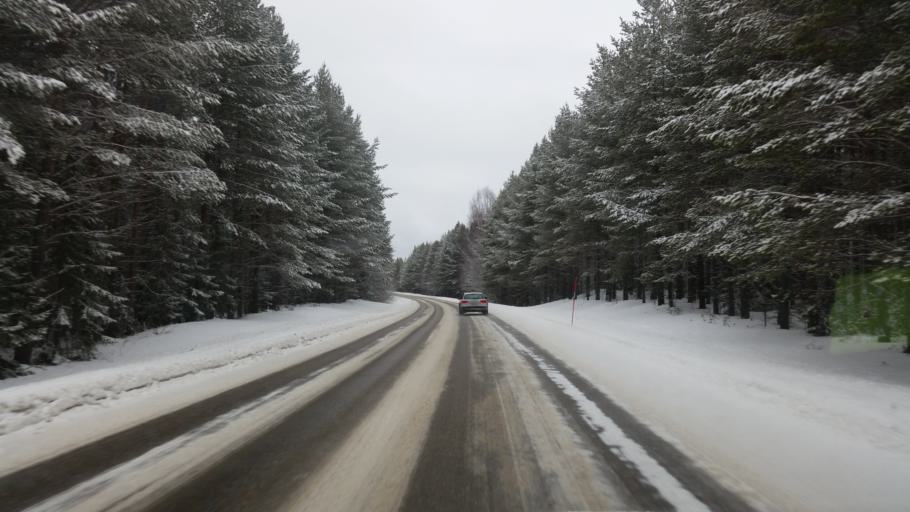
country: SE
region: Vaesternorrland
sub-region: Ange Kommun
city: Ange
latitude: 62.0874
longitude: 15.0940
